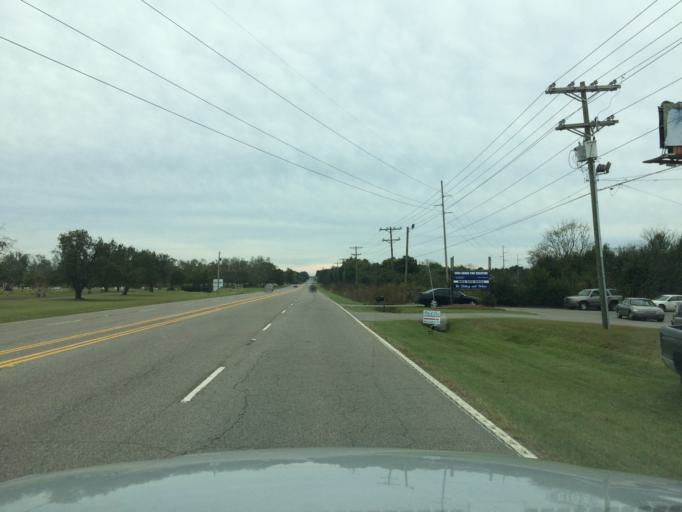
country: US
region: South Carolina
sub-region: Aiken County
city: New Ellenton
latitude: 33.4578
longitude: -81.6871
